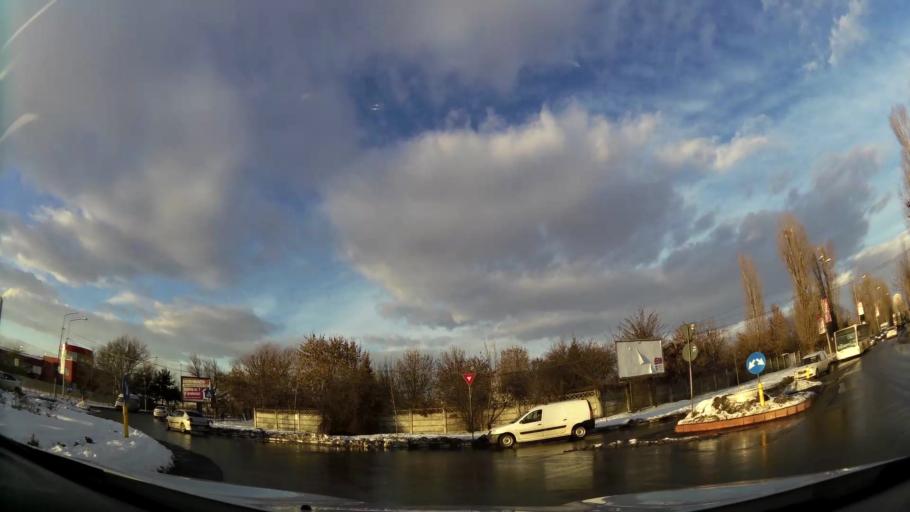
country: RO
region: Ilfov
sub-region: Comuna Popesti-Leordeni
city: Popesti-Leordeni
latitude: 44.3646
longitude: 26.1265
